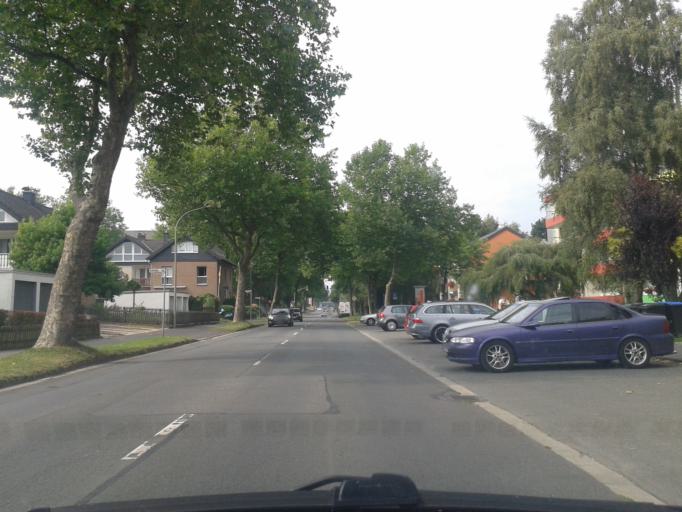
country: DE
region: North Rhine-Westphalia
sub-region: Regierungsbezirk Detmold
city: Paderborn
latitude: 51.7424
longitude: 8.7598
